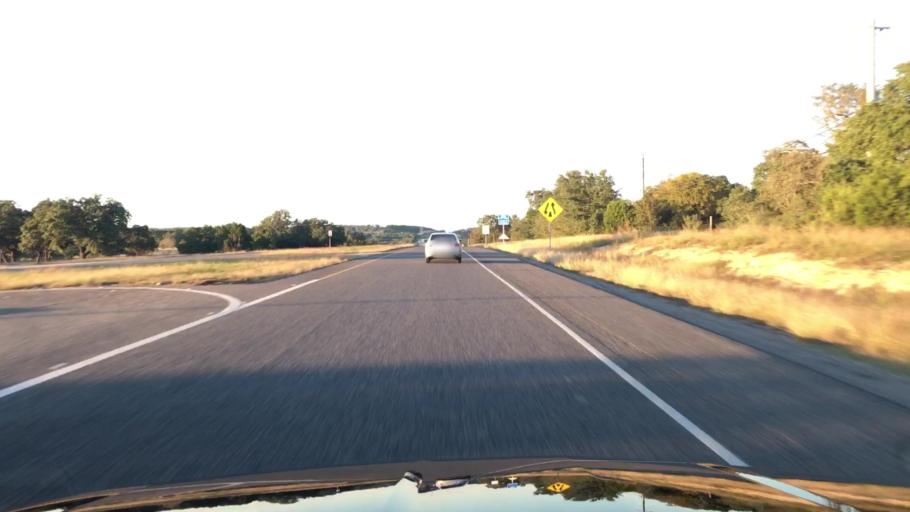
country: US
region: Texas
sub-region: Blanco County
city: Blanco
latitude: 29.9413
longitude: -98.4103
